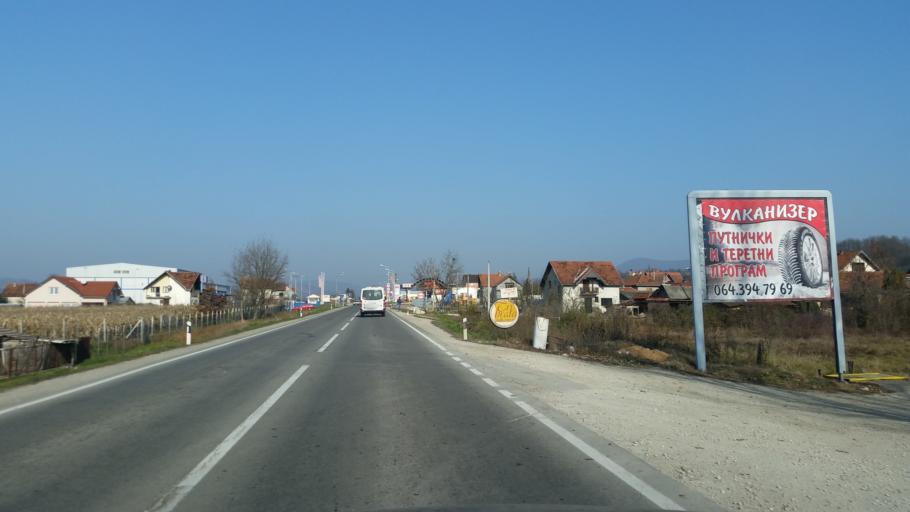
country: RS
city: Prislonica
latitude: 43.9228
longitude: 20.4091
